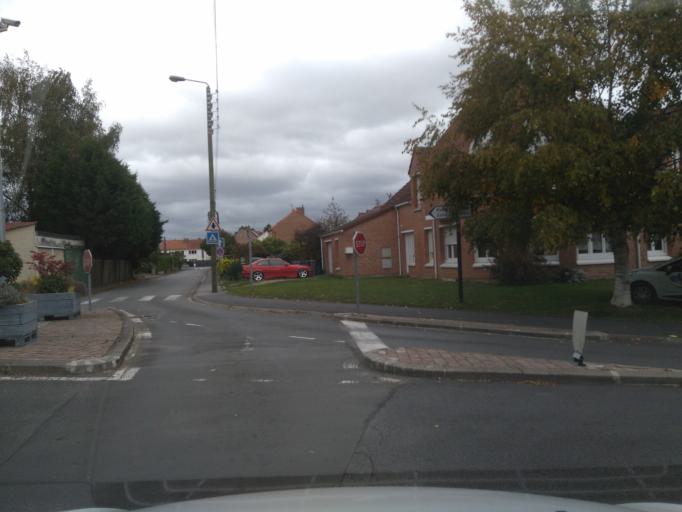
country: FR
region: Nord-Pas-de-Calais
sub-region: Departement du Nord
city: Saint-Saulve
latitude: 50.3689
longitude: 3.5621
